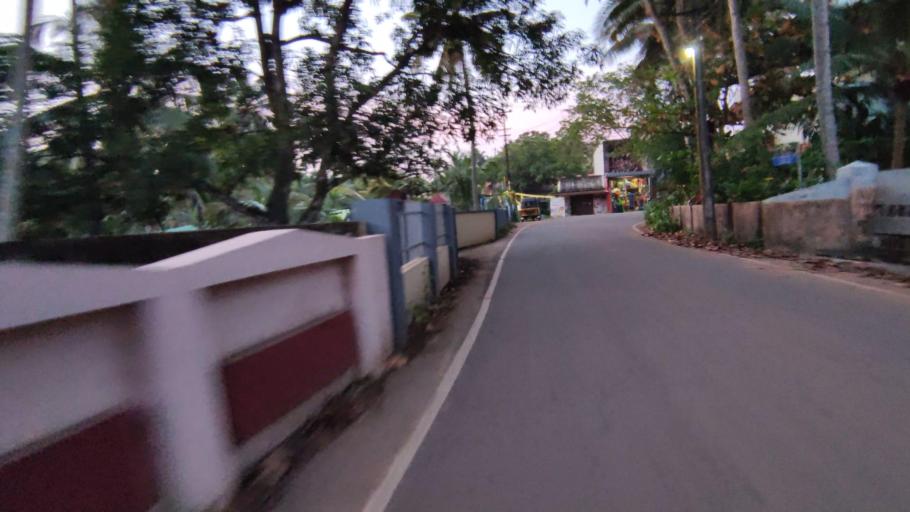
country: IN
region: Kerala
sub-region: Kottayam
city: Kottayam
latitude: 9.5819
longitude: 76.4354
